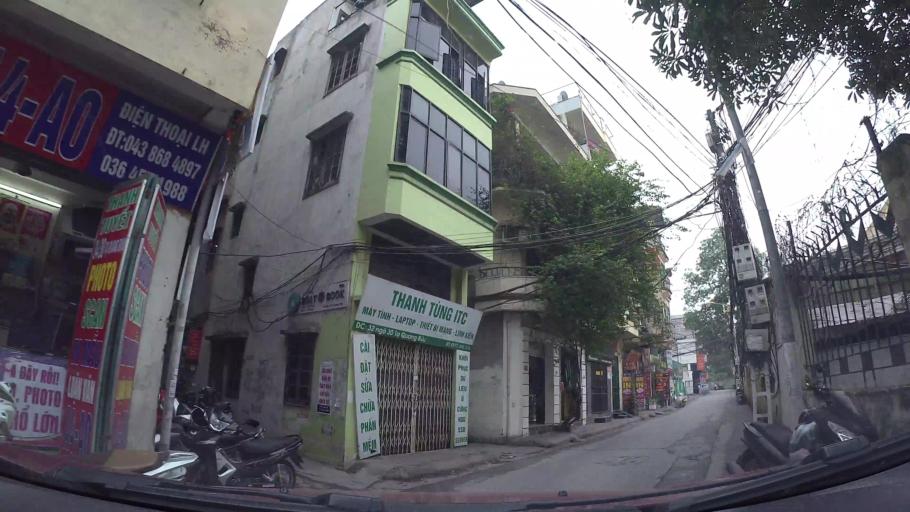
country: VN
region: Ha Noi
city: Hai BaTrung
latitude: 21.0067
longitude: 105.8458
